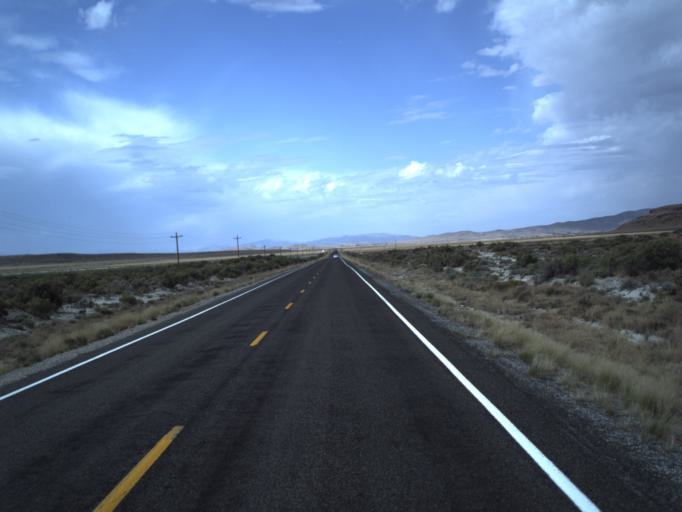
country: US
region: Utah
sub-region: Tooele County
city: Wendover
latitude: 41.4231
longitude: -113.8741
